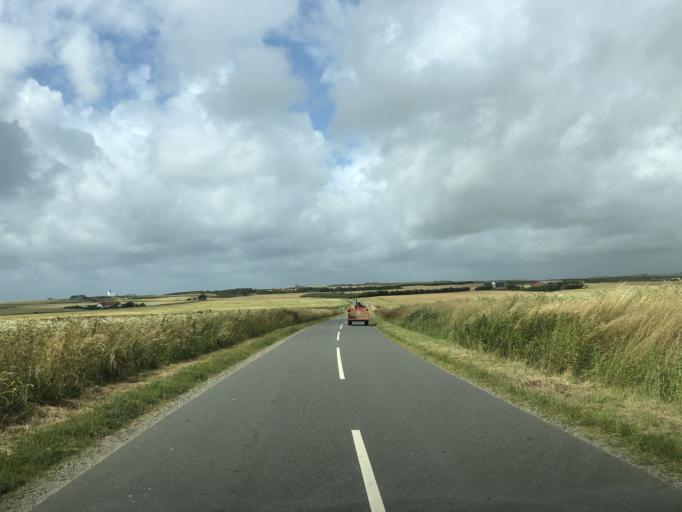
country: DK
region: Central Jutland
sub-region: Lemvig Kommune
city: Harboore
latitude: 56.4858
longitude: 8.1397
